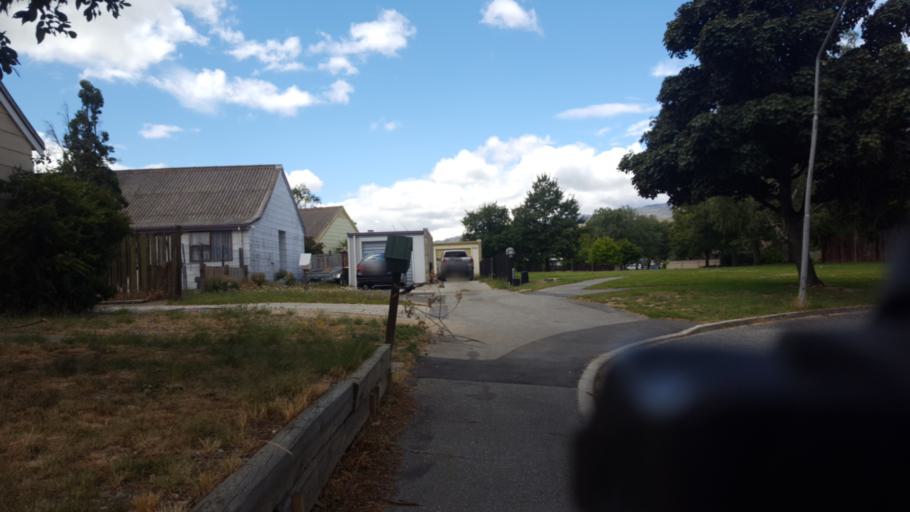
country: NZ
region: Otago
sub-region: Queenstown-Lakes District
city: Wanaka
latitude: -45.0404
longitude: 169.1833
